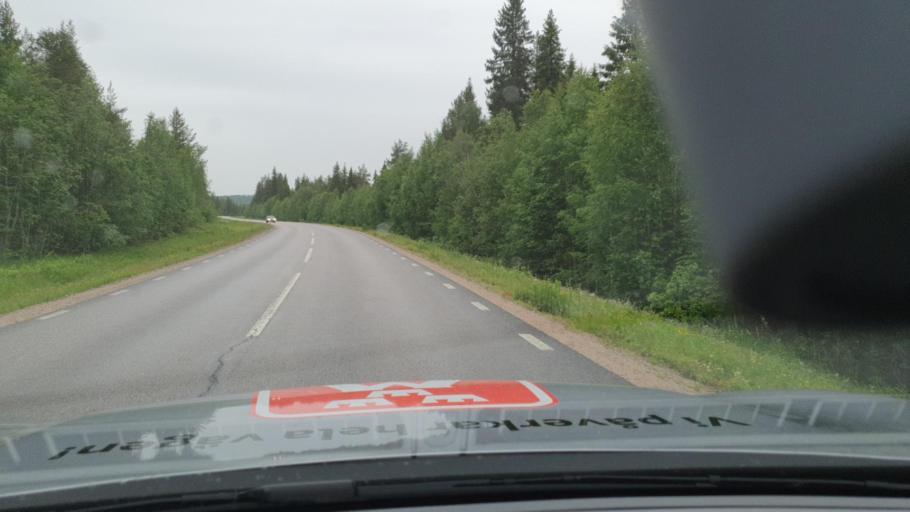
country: SE
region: Norrbotten
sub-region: Overtornea Kommun
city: OEvertornea
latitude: 66.4073
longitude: 23.4687
